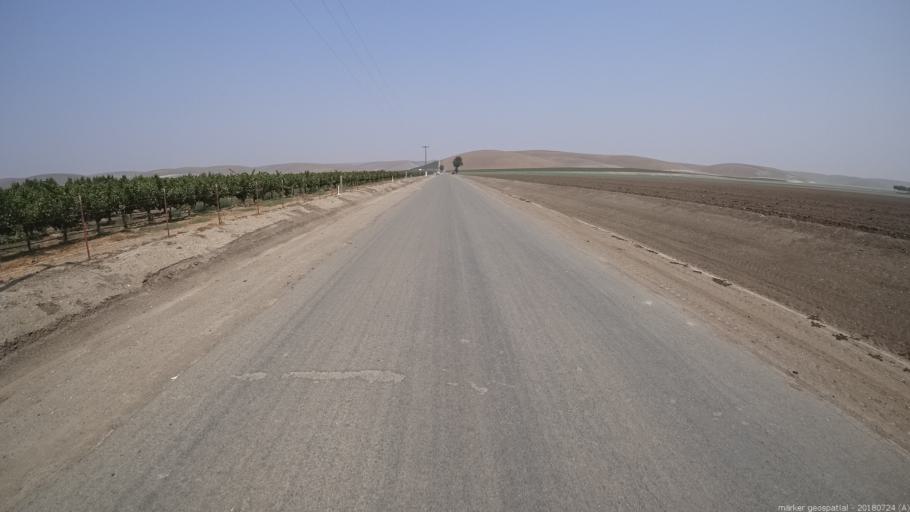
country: US
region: California
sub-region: Monterey County
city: King City
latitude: 36.1925
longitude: -121.0649
